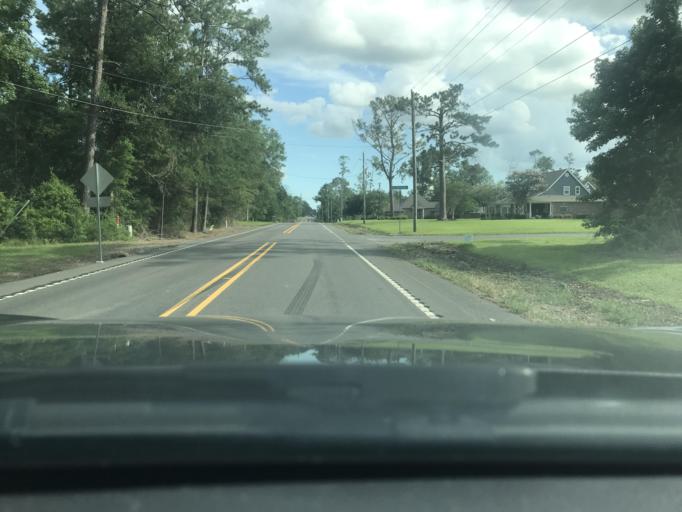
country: US
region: Louisiana
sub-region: Calcasieu Parish
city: Moss Bluff
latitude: 30.3384
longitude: -93.2581
